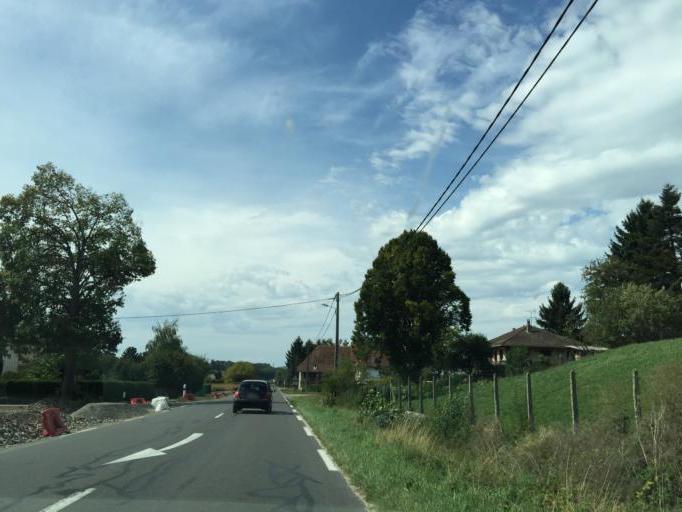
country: FR
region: Rhone-Alpes
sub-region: Departement de l'Isere
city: Saint-Didier-de-la-Tour
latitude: 45.5564
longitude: 5.4774
